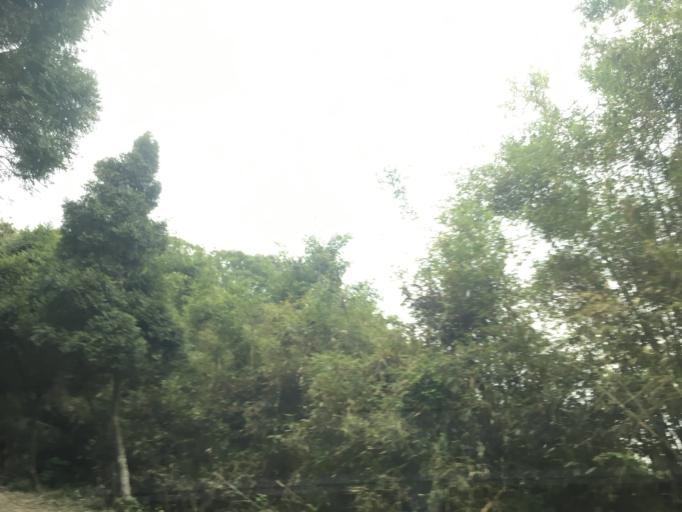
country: TW
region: Taiwan
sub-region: Nantou
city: Puli
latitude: 23.9697
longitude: 120.8336
